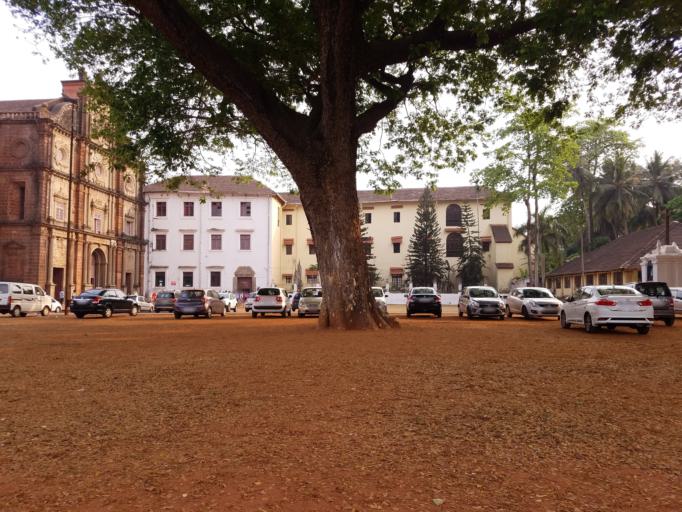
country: IN
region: Goa
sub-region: North Goa
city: Jua
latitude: 15.5016
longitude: 73.9112
